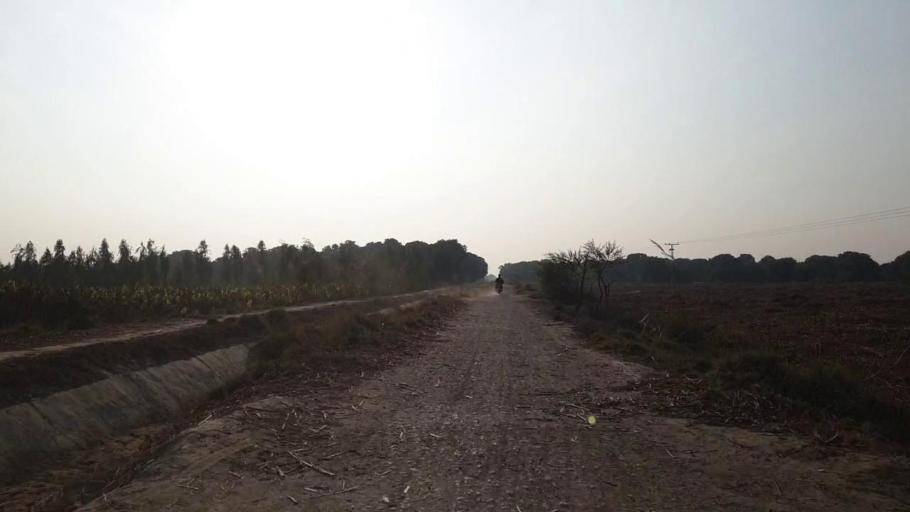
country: PK
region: Sindh
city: Matiari
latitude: 25.5891
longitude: 68.4607
